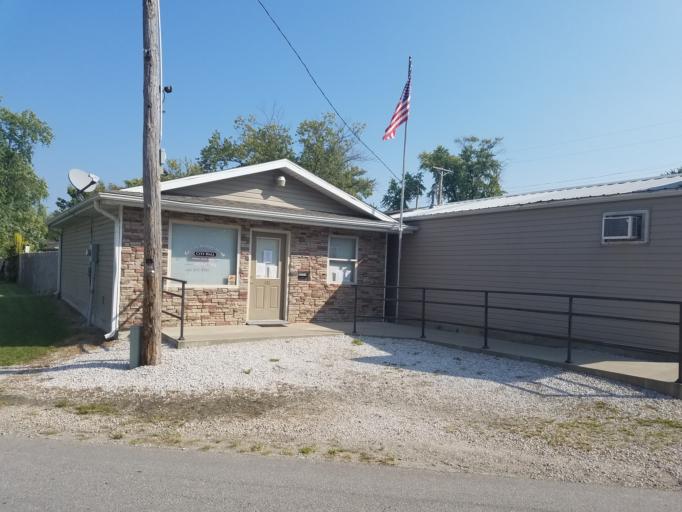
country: US
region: Missouri
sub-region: Moniteau County
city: California
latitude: 38.8136
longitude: -92.5914
